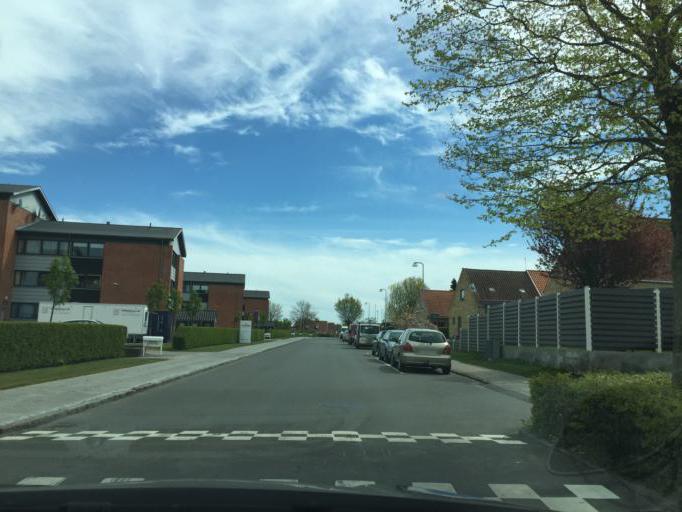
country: DK
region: South Denmark
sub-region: Odense Kommune
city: Odense
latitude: 55.4076
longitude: 10.3373
